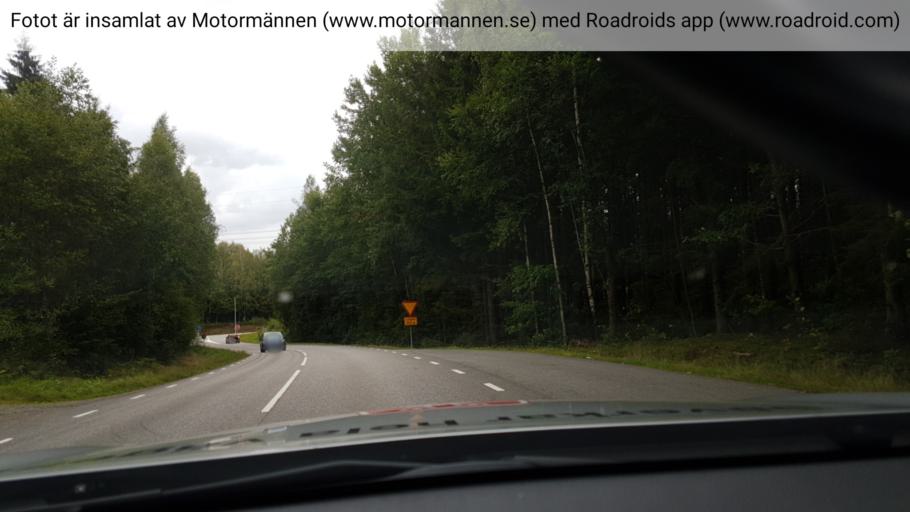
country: SE
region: Vaestra Goetaland
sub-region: Harryda Kommun
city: Hindas
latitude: 57.6204
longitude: 12.4201
